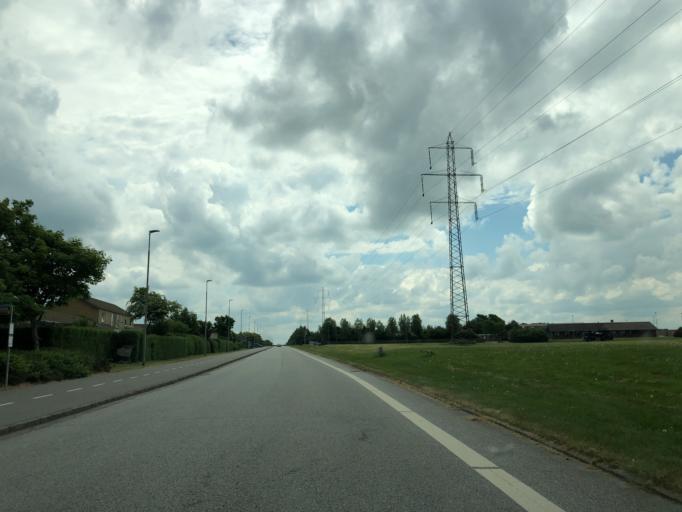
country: DK
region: Central Jutland
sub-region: Struer Kommune
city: Struer
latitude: 56.4792
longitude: 8.5873
